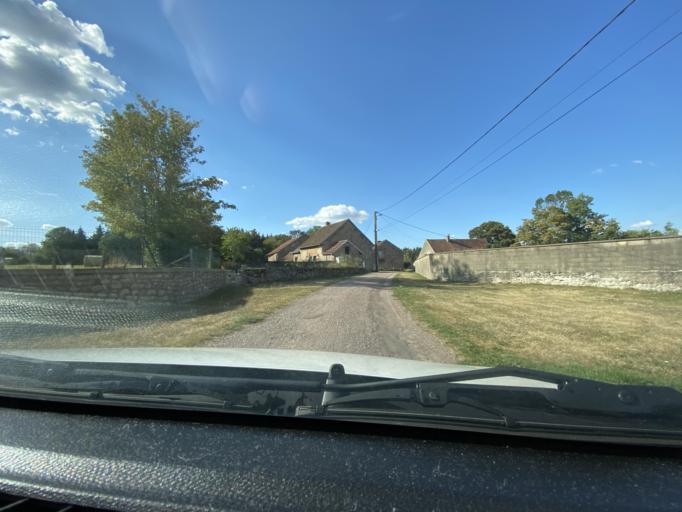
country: FR
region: Bourgogne
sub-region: Departement de la Cote-d'Or
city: Saulieu
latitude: 47.3174
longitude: 4.2025
